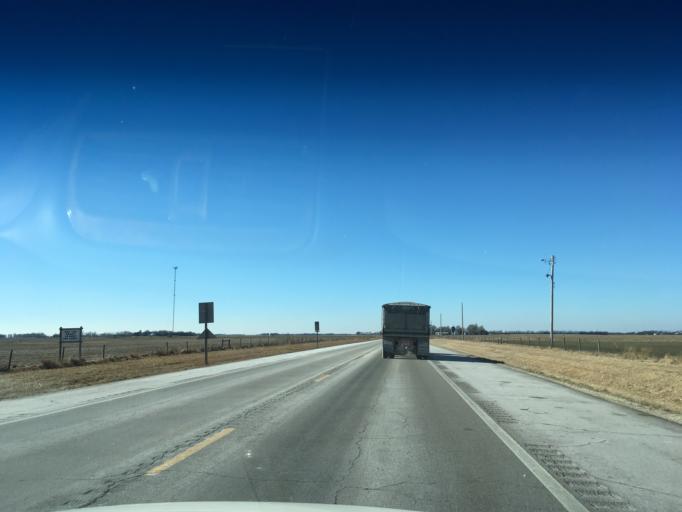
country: US
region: Kansas
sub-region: Harvey County
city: Halstead
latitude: 38.0286
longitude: -97.5551
